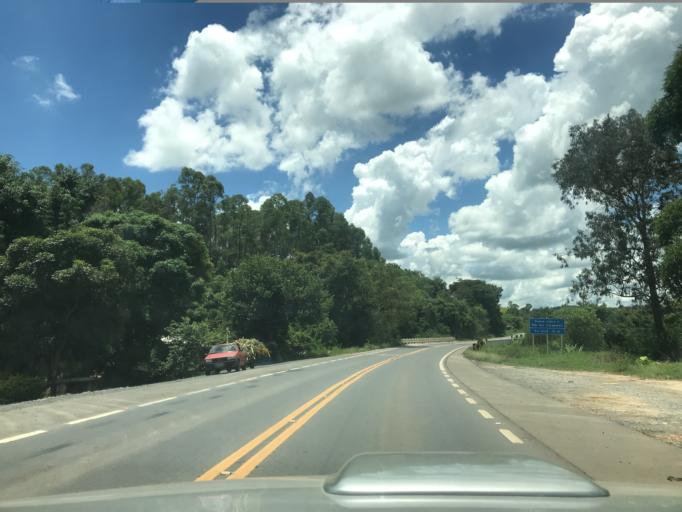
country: BR
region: Minas Gerais
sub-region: Perdoes
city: Perdoes
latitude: -21.0951
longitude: -45.1012
